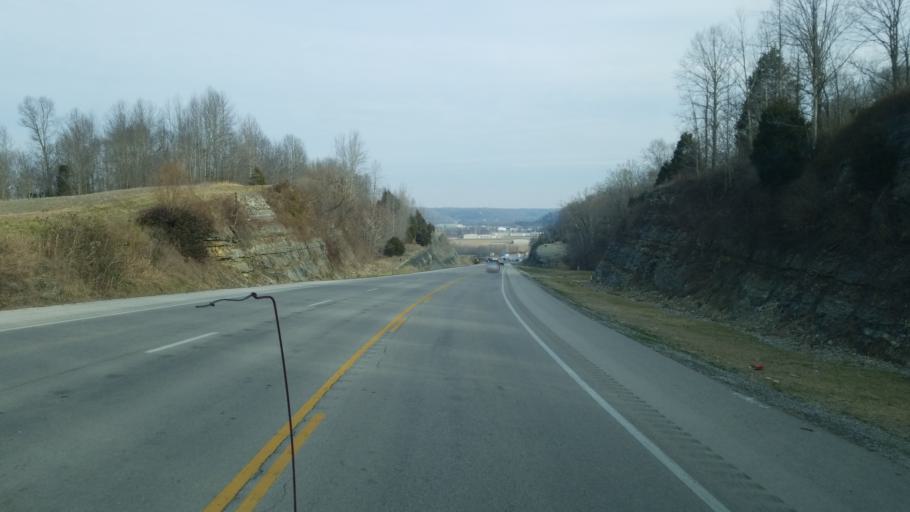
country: US
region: Kentucky
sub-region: Casey County
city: Liberty
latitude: 37.2853
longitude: -84.9588
